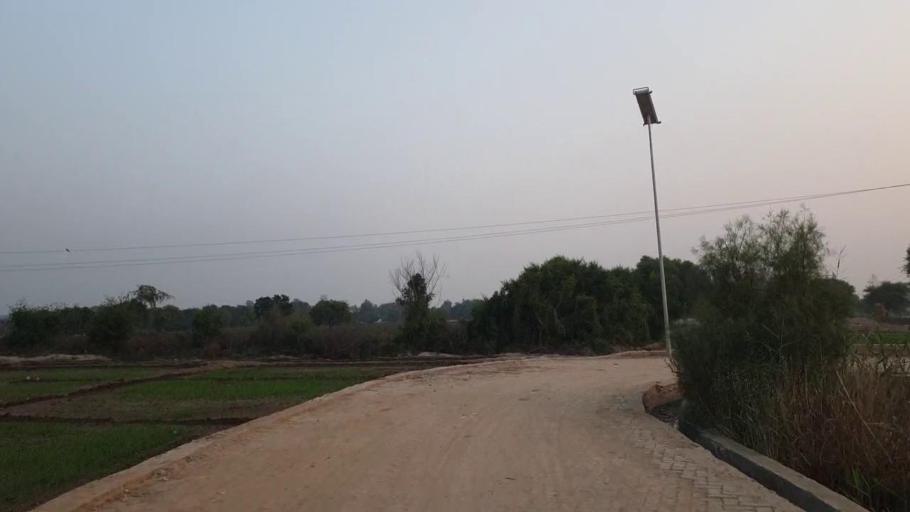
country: PK
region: Sindh
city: Bhan
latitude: 26.5212
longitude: 67.7119
